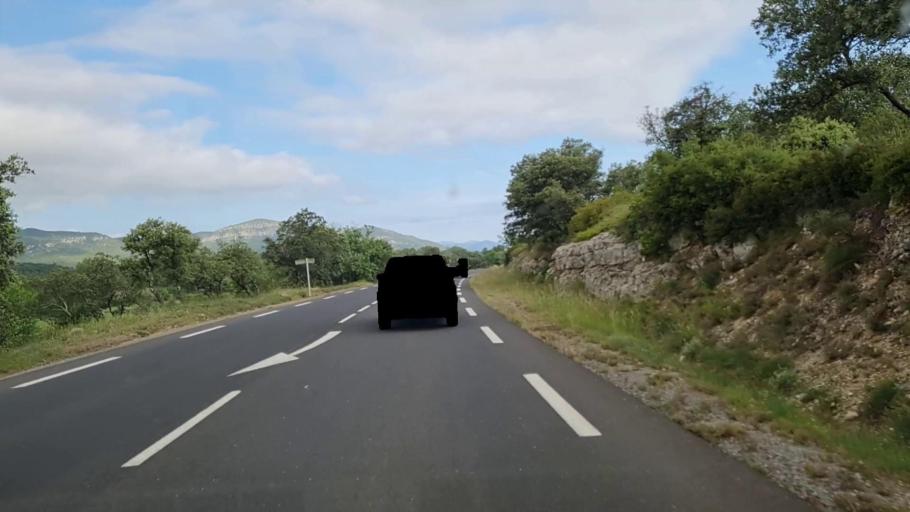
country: FR
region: Languedoc-Roussillon
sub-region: Departement du Gard
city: Quissac
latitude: 43.8876
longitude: 4.0156
